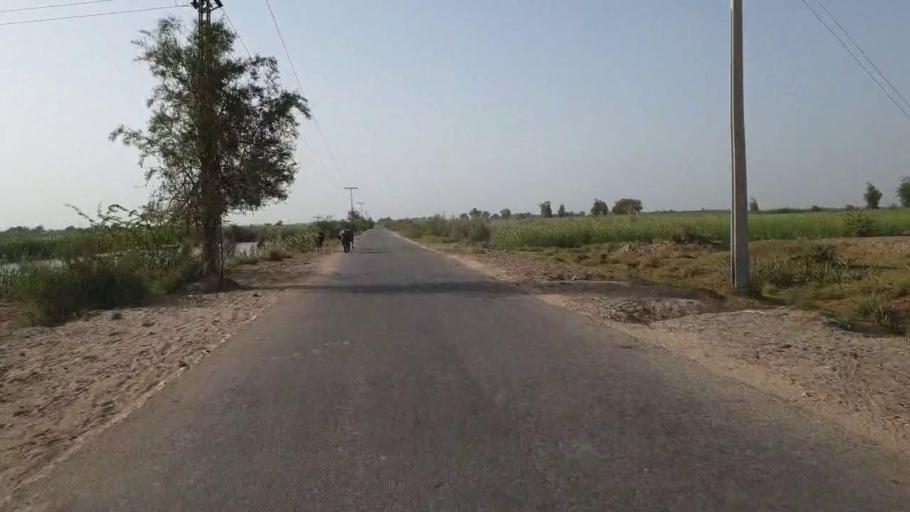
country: PK
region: Sindh
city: Jam Sahib
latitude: 26.3962
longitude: 68.8787
